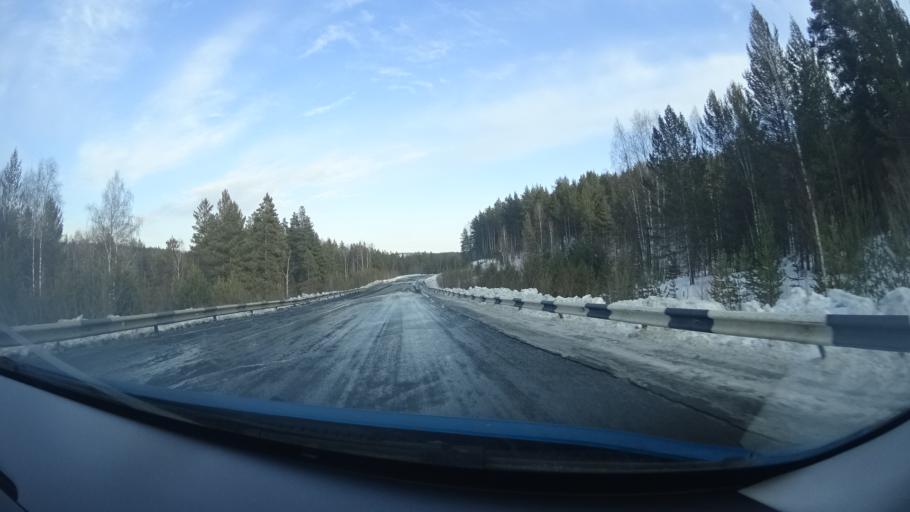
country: RU
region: Bashkortostan
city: Lomovka
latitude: 53.5240
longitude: 58.2834
